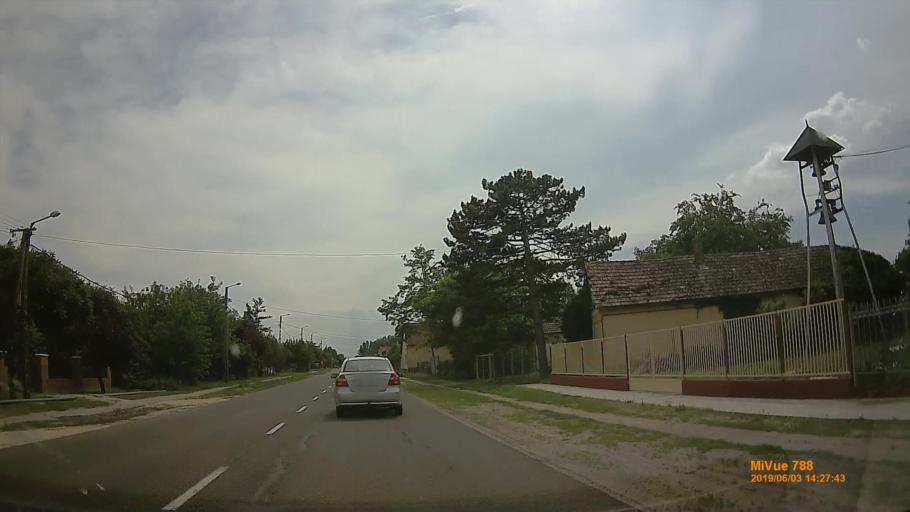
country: HU
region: Bacs-Kiskun
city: Tiszakecske
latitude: 46.9838
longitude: 20.1161
